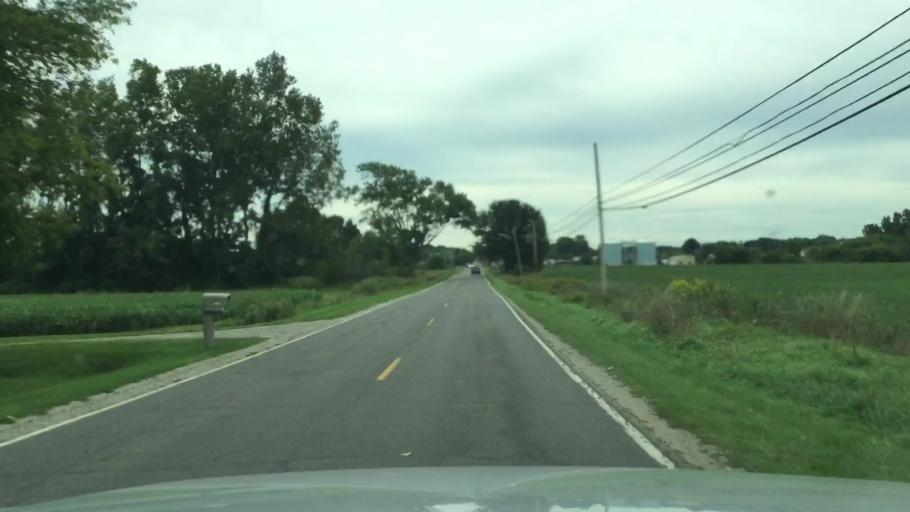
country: US
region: Michigan
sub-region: Shiawassee County
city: Durand
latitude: 42.9312
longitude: -83.9884
